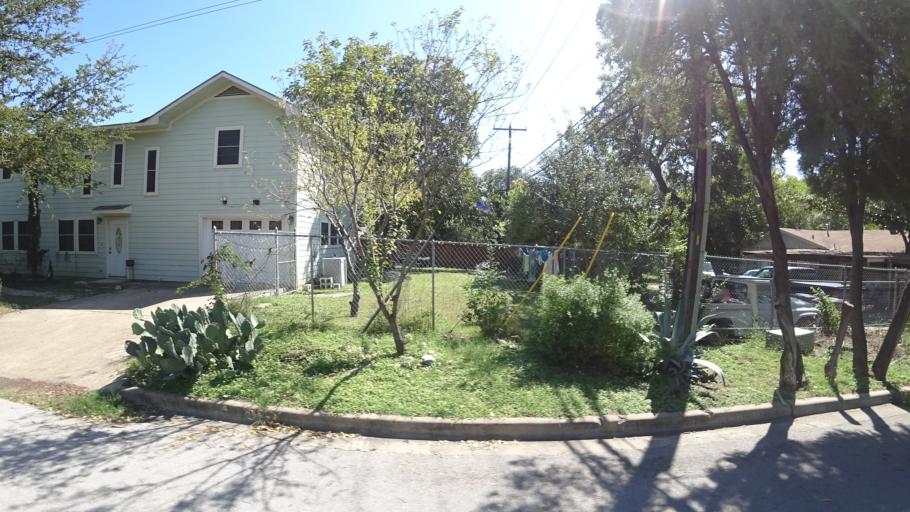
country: US
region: Texas
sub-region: Travis County
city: Austin
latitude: 30.3094
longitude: -97.6991
